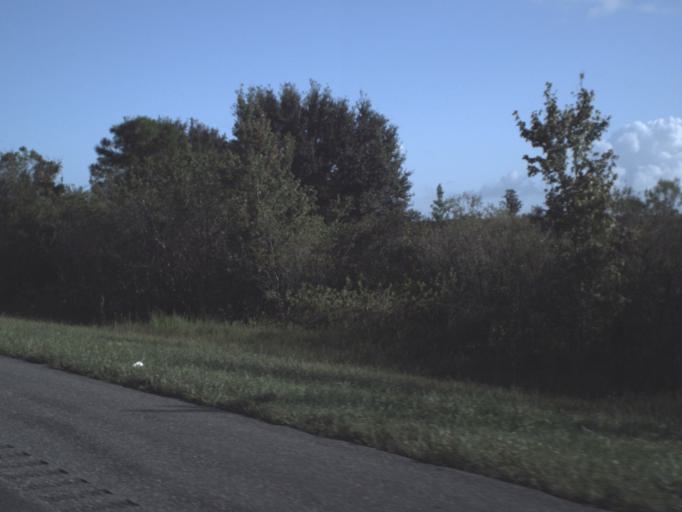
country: US
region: Florida
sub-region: Brevard County
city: June Park
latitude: 27.8362
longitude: -81.0055
